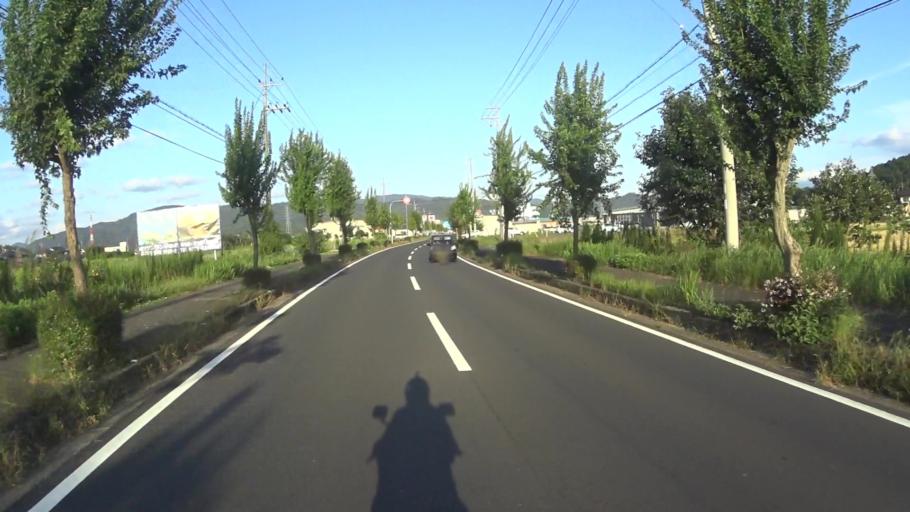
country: JP
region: Kyoto
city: Miyazu
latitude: 35.6090
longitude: 135.0635
